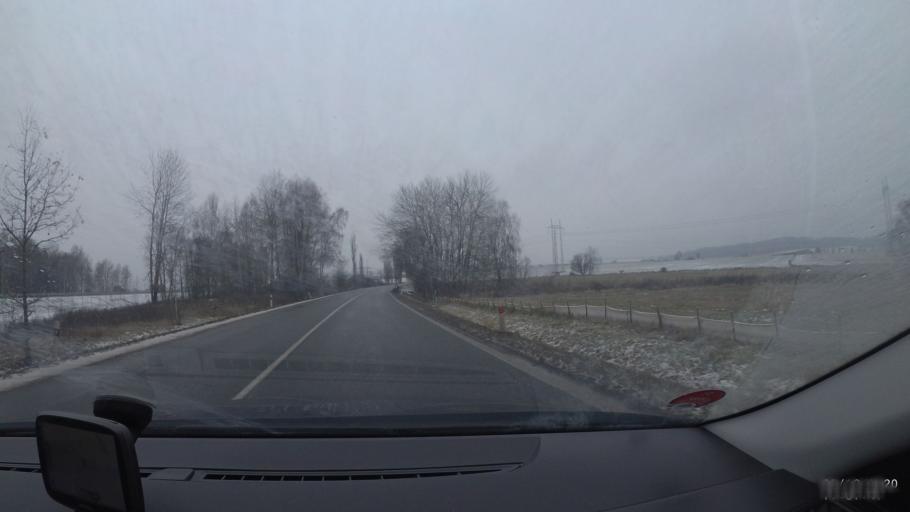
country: CZ
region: Central Bohemia
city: Revnicov
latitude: 50.1759
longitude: 13.8225
